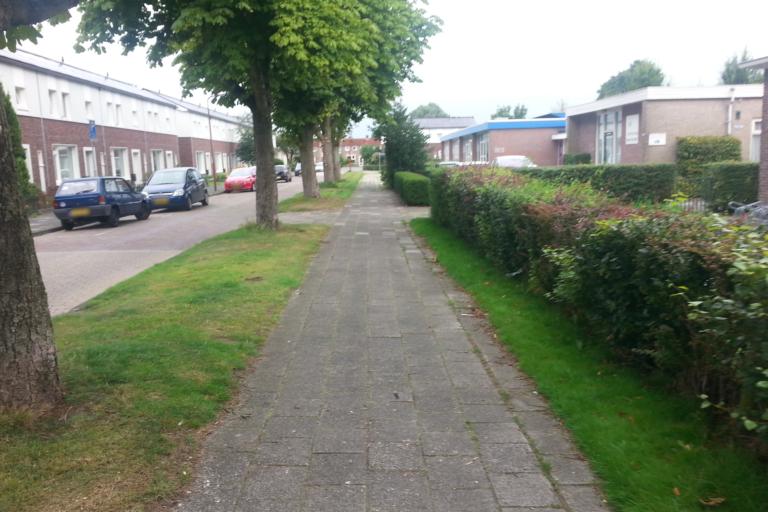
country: NL
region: Friesland
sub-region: Gemeente Heerenveen
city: Heerenveen
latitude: 52.9574
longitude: 5.9219
